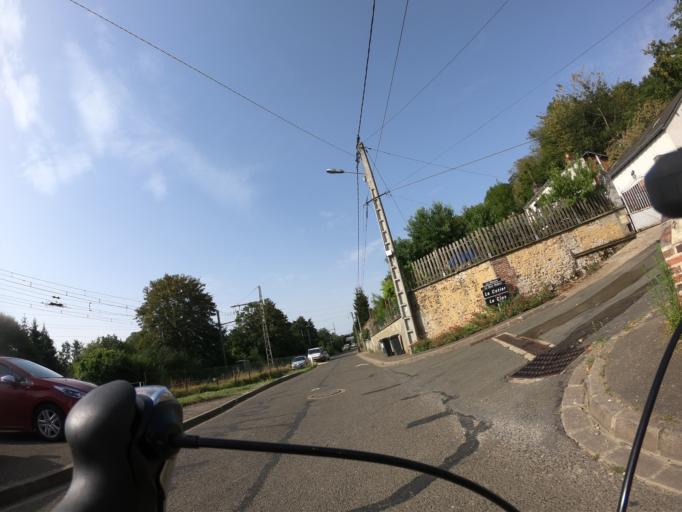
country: FR
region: Centre
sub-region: Departement d'Eure-et-Loir
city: Margon
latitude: 48.3367
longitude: 0.8194
